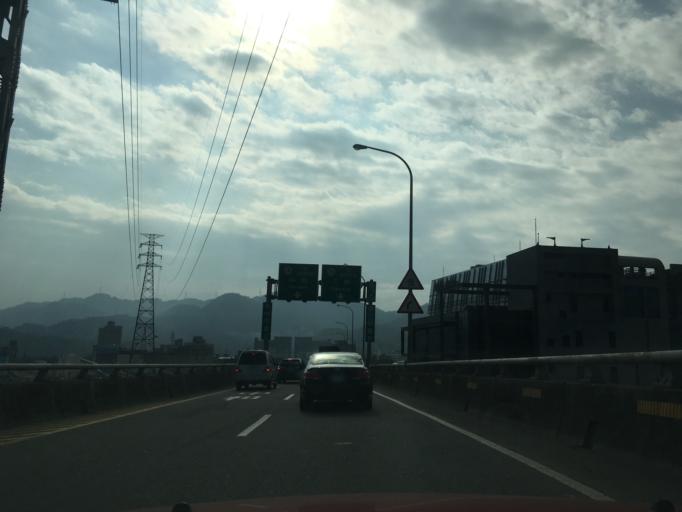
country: TW
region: Taipei
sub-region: Taipei
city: Banqiao
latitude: 24.9720
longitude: 121.4326
